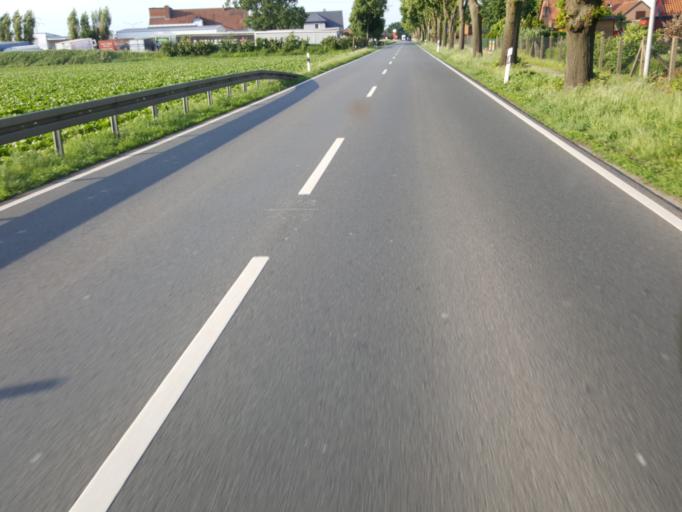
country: DE
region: Lower Saxony
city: Leese
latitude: 52.5139
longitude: 9.1187
